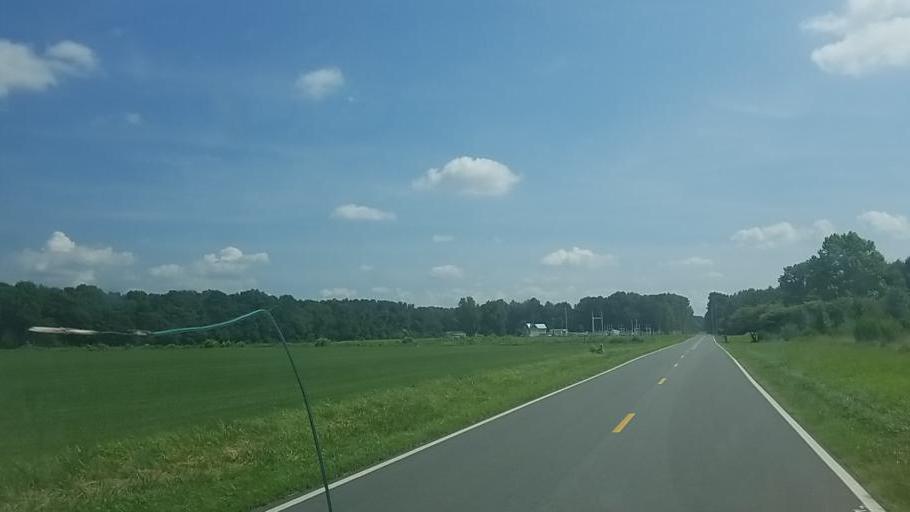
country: US
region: Maryland
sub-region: Wicomico County
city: Hebron
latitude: 38.4279
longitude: -75.6977
